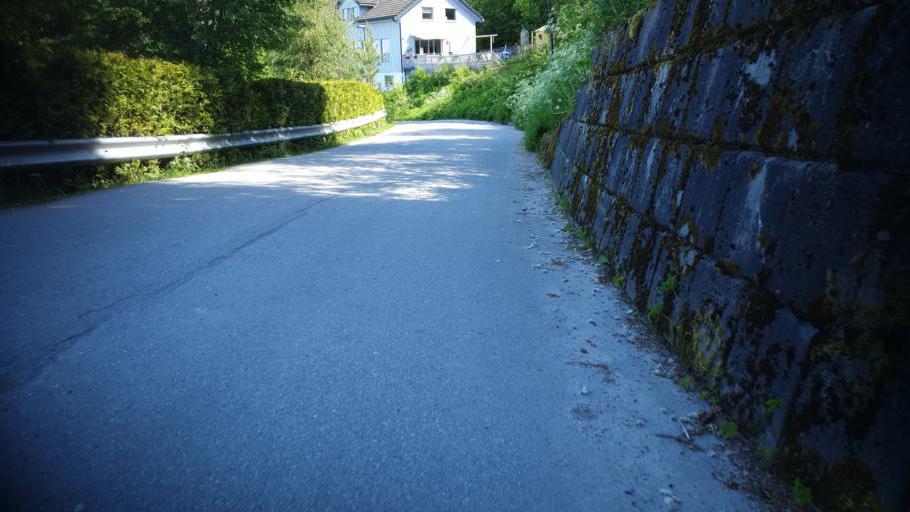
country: NO
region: Sor-Trondelag
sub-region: Malvik
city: Malvik
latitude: 63.4362
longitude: 10.6231
